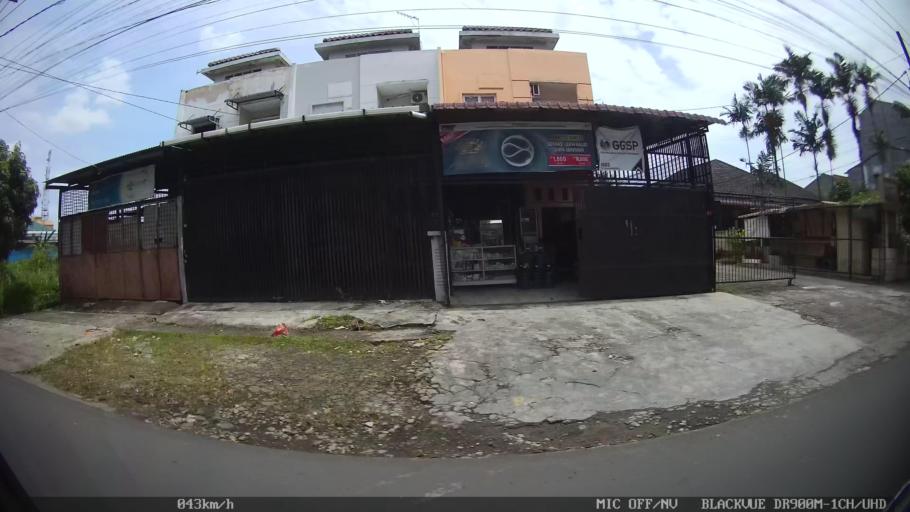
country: ID
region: North Sumatra
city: Sunggal
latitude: 3.5550
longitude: 98.6358
